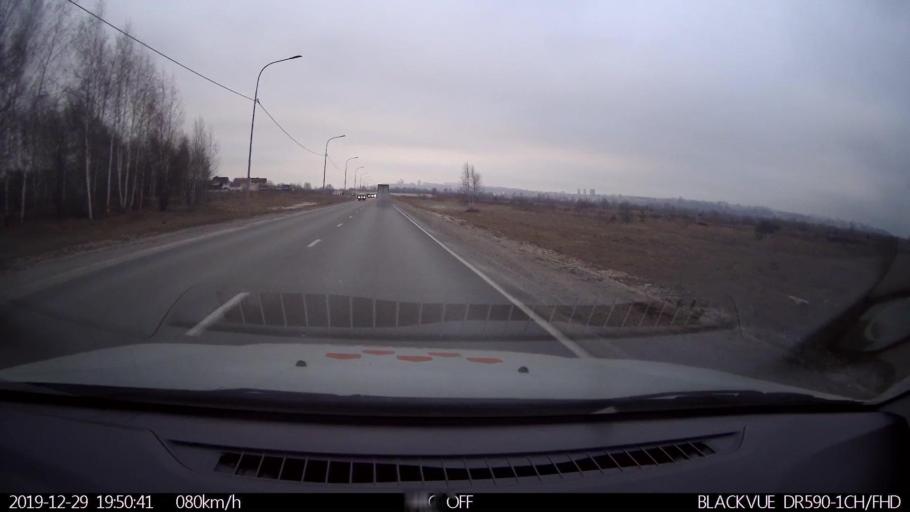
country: RU
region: Nizjnij Novgorod
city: Bor
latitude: 56.3655
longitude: 44.0304
